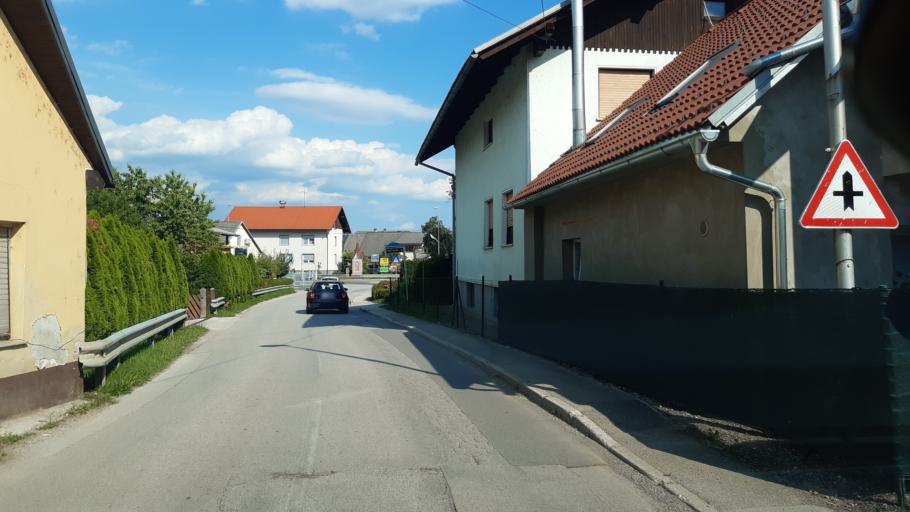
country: SI
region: Sencur
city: Hrastje
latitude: 46.2124
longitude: 14.3956
